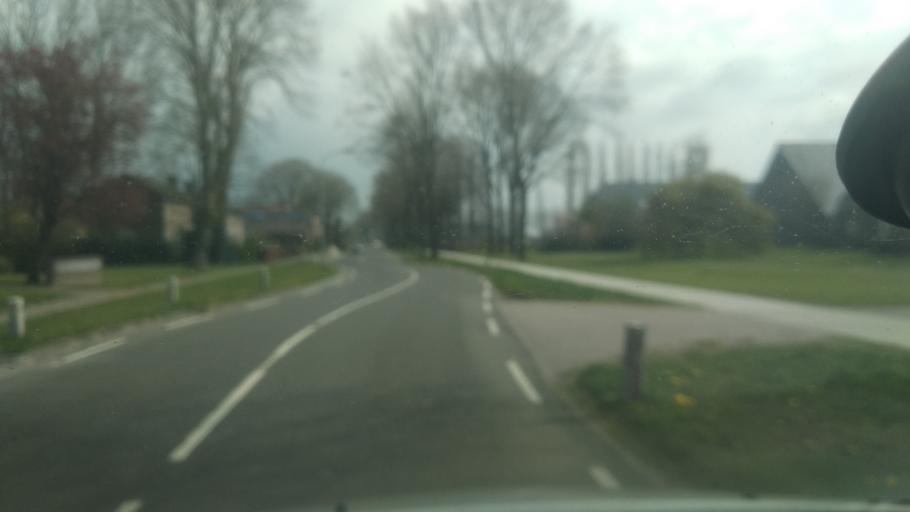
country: NL
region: Groningen
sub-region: Gemeente Stadskanaal
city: Stadskanaal
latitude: 52.9119
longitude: 6.9432
